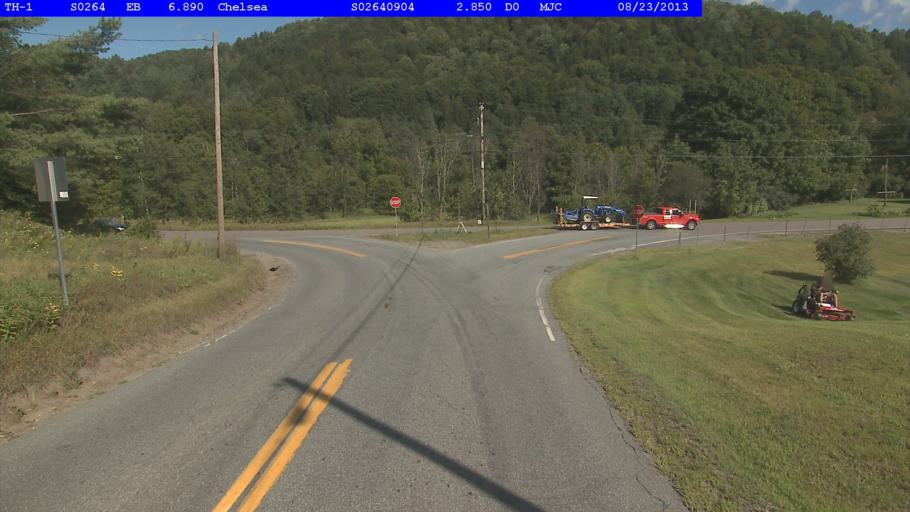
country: US
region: Vermont
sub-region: Orange County
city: Chelsea
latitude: 43.9619
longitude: -72.4649
